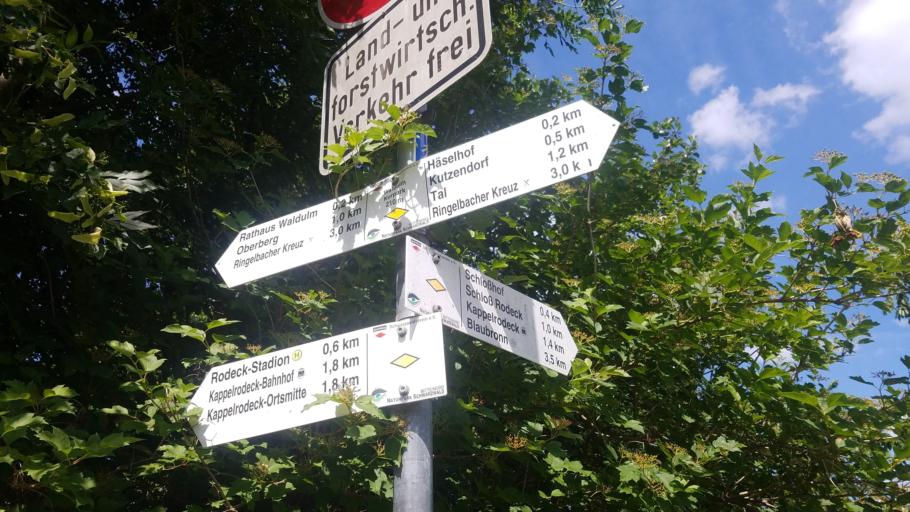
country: DE
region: Baden-Wuerttemberg
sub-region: Freiburg Region
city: Kappelrodeck
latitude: 48.5852
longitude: 8.1045
